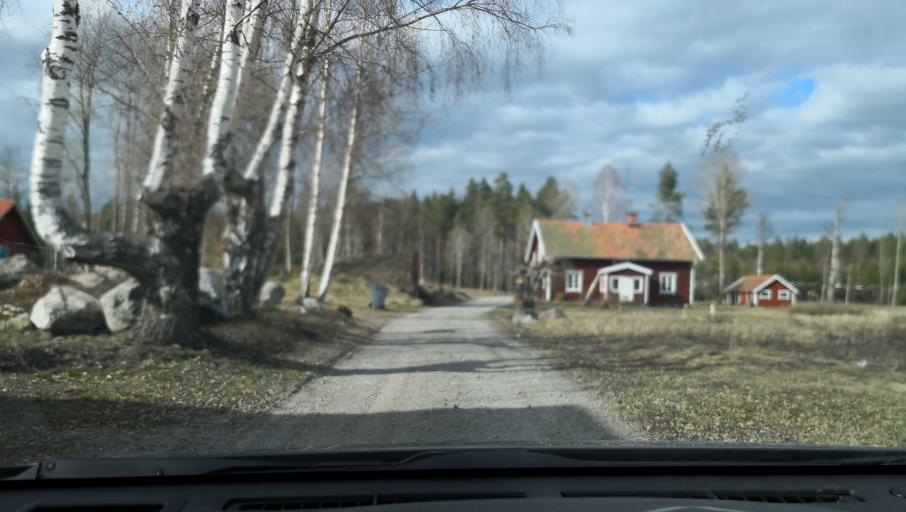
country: SE
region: Soedermanland
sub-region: Katrineholms Kommun
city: Katrineholm
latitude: 59.1262
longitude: 16.1448
